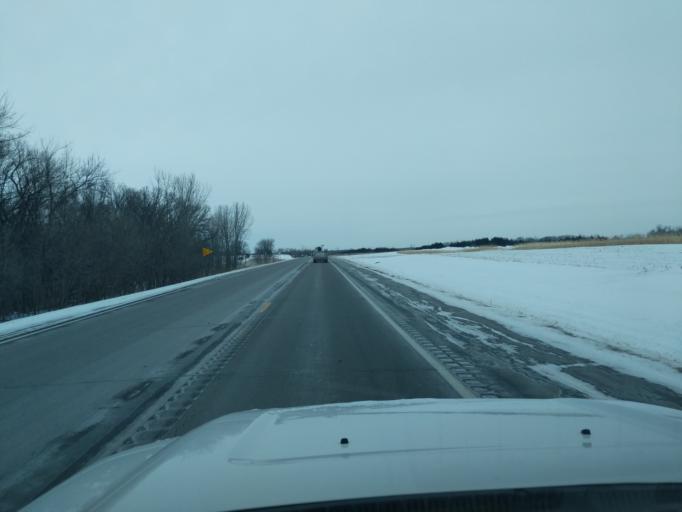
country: US
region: Minnesota
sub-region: Redwood County
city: Redwood Falls
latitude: 44.5656
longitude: -94.9961
